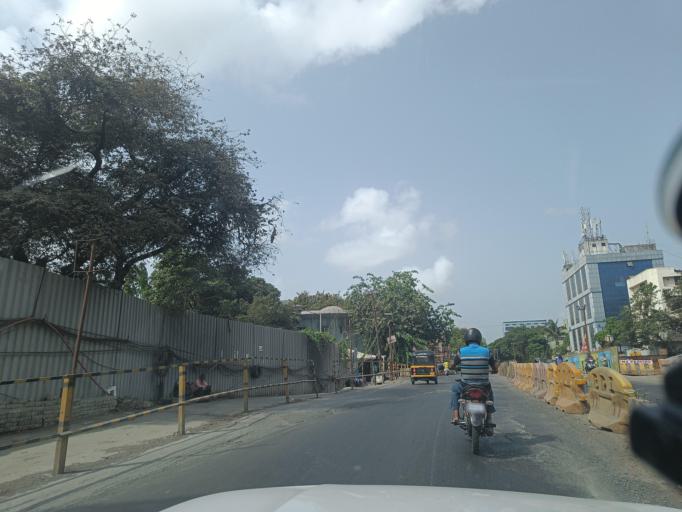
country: IN
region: Maharashtra
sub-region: Mumbai Suburban
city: Powai
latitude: 19.1257
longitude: 72.8735
